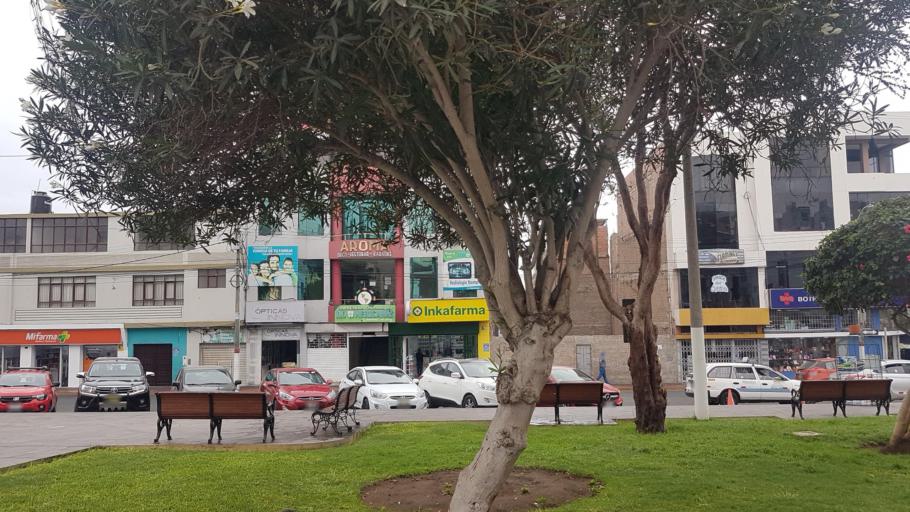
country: PE
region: Moquegua
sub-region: Provincia de Ilo
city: Ilo
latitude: -17.6463
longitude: -71.3451
